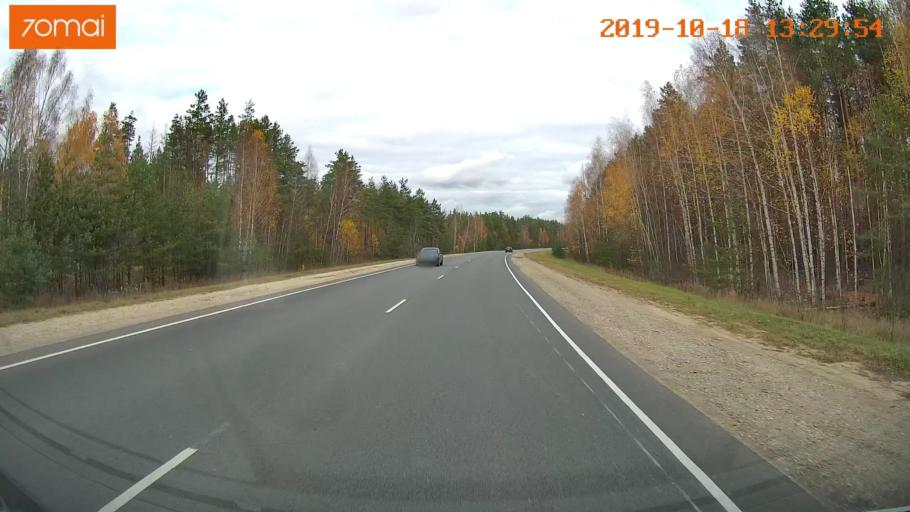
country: RU
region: Rjazan
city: Solotcha
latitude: 54.8022
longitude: 39.8783
